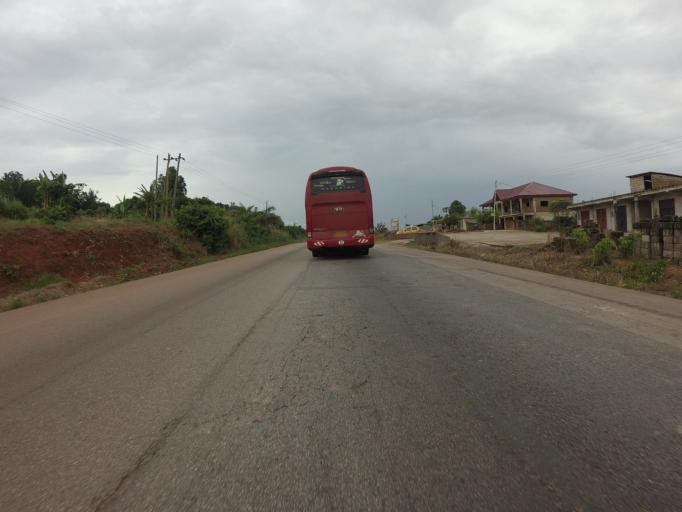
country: GH
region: Ashanti
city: Konongo
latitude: 6.6172
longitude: -1.1810
